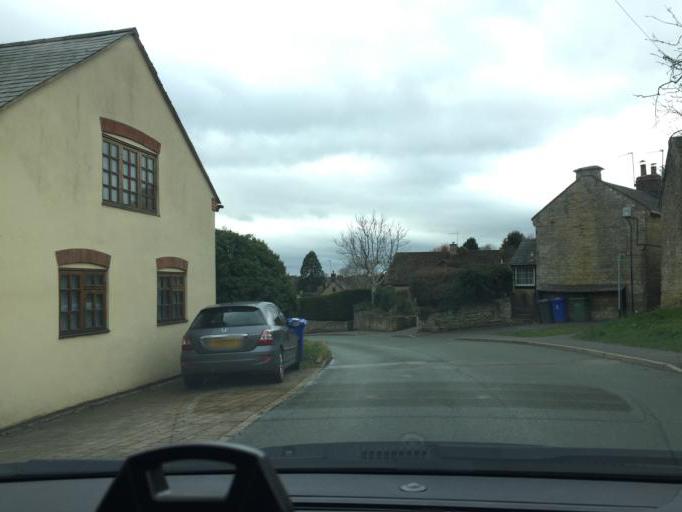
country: GB
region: England
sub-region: Northamptonshire
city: Brackley
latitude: 52.0928
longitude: -1.1398
